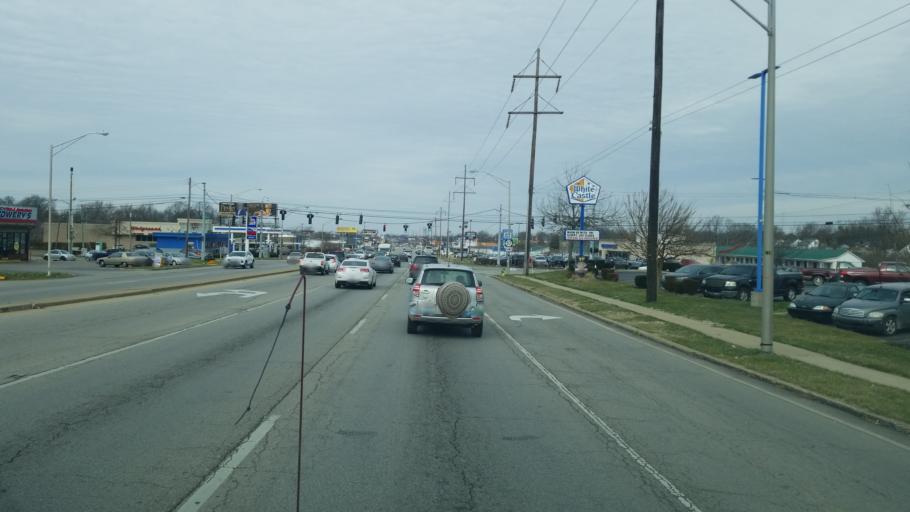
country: US
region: Kentucky
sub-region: Fayette County
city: Lexington-Fayette
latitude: 38.0594
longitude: -84.4642
